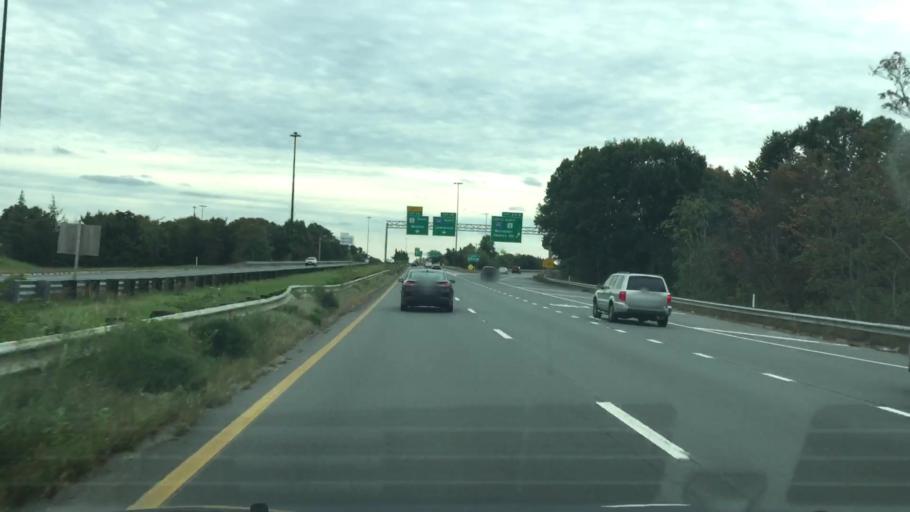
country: US
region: Massachusetts
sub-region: Middlesex County
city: Lowell
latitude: 42.6160
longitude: -71.3204
